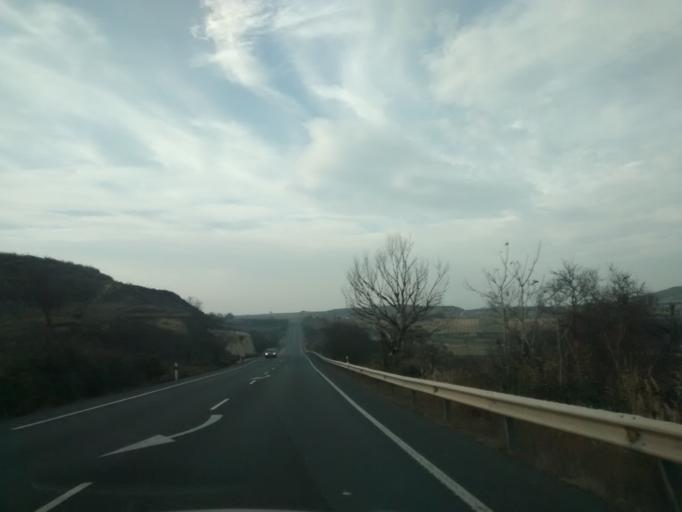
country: ES
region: La Rioja
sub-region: Provincia de La Rioja
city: Briones
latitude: 42.5442
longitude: -2.7924
